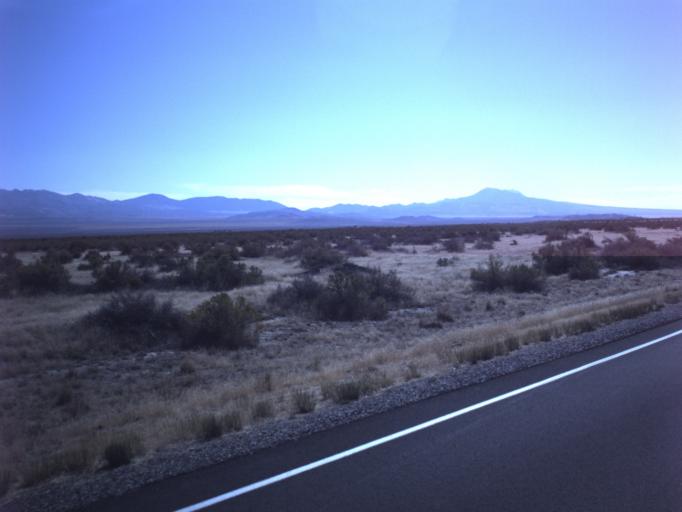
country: US
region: Utah
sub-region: Tooele County
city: Grantsville
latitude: 40.2692
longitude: -112.7413
